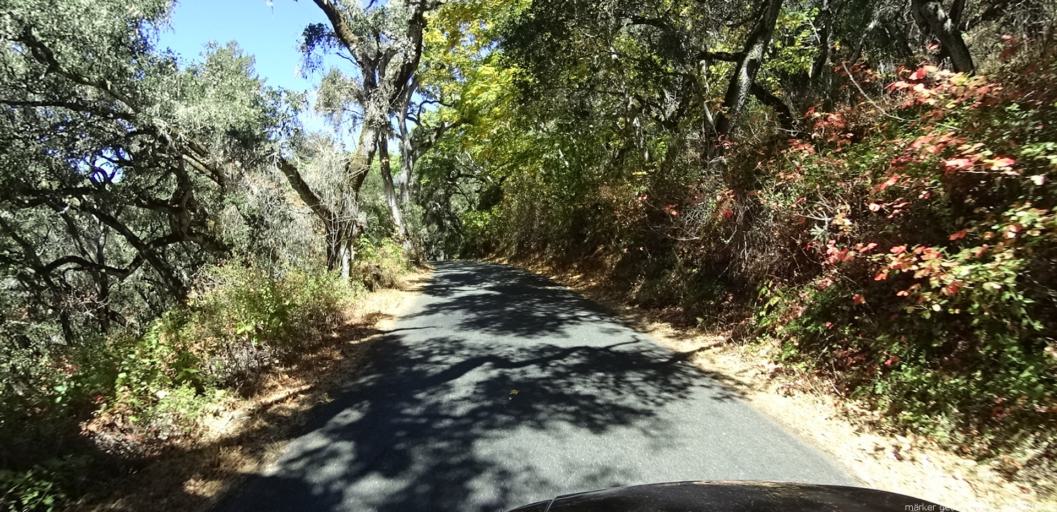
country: US
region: California
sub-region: Monterey County
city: Carmel Valley Village
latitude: 36.4977
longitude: -121.8108
